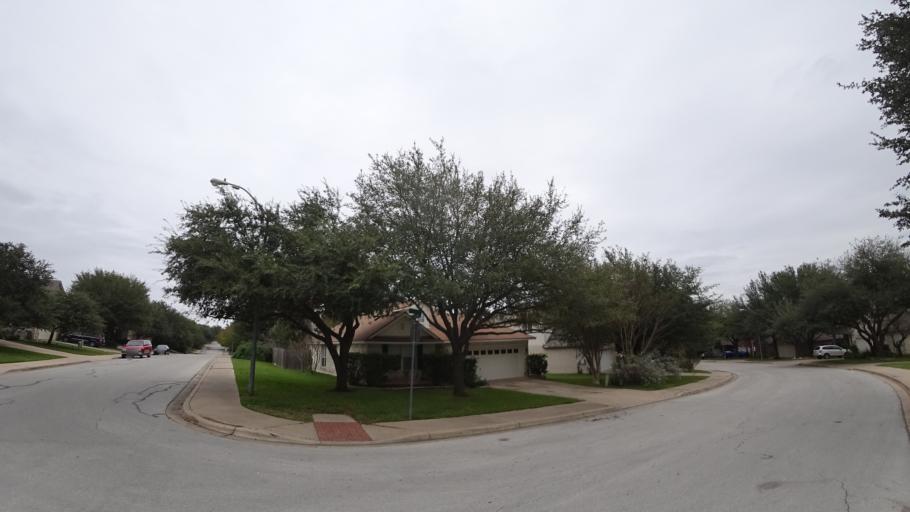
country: US
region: Texas
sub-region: Travis County
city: Wells Branch
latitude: 30.4483
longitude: -97.6841
